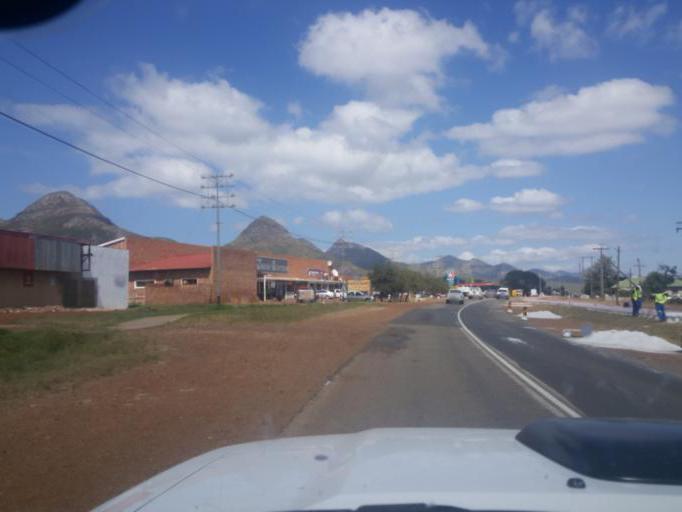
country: ZA
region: Eastern Cape
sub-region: Cacadu District Municipality
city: Kareedouw
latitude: -33.9527
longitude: 24.2974
